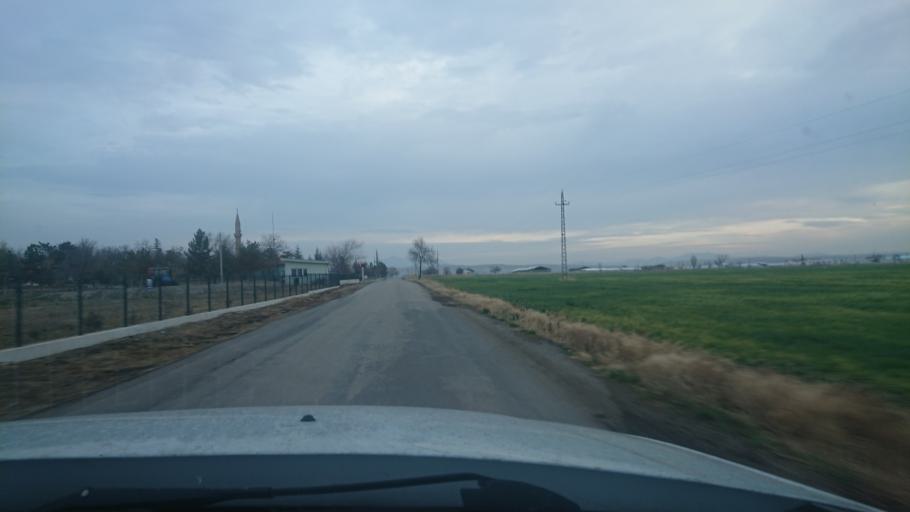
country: TR
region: Aksaray
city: Yesilova
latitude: 38.4559
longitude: 33.8394
